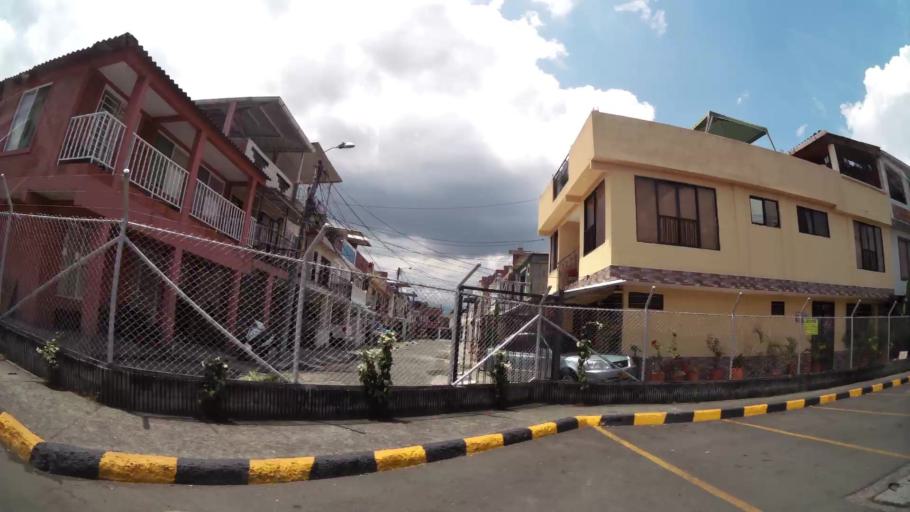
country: CO
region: Valle del Cauca
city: Cali
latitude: 3.4694
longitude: -76.4821
